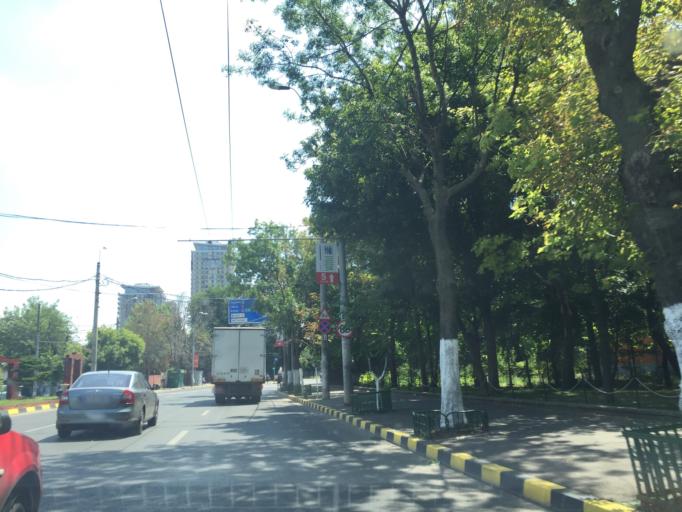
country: RO
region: Bucuresti
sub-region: Municipiul Bucuresti
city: Bucharest
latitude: 44.4082
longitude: 26.1191
